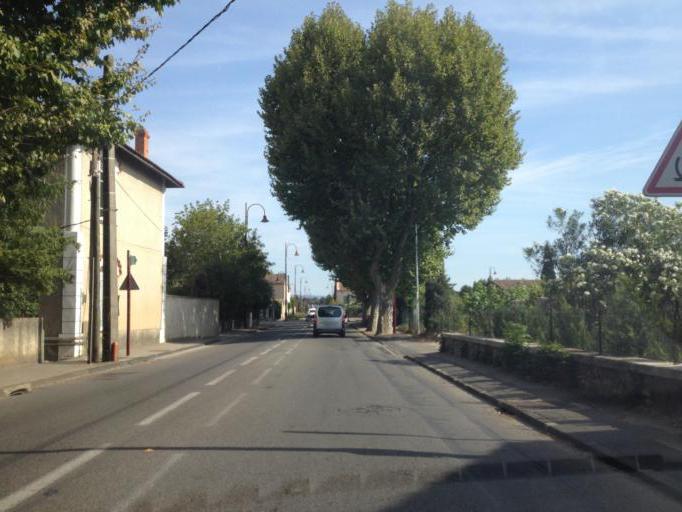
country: FR
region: Provence-Alpes-Cote d'Azur
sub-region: Departement du Vaucluse
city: Aubignan
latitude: 44.0964
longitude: 5.0260
